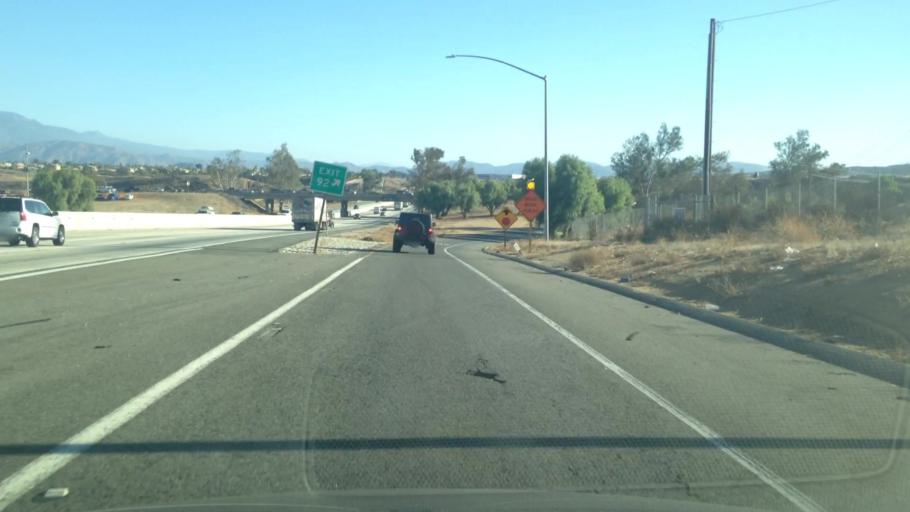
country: US
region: California
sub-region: Riverside County
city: Beaumont
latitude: 33.9470
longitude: -117.0053
